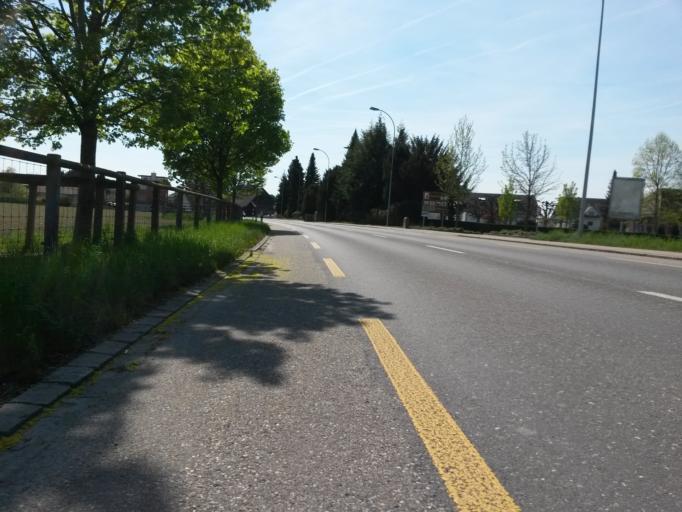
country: CH
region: Bern
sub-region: Oberaargau
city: Herzogenbuchsee
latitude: 47.1943
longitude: 7.7119
